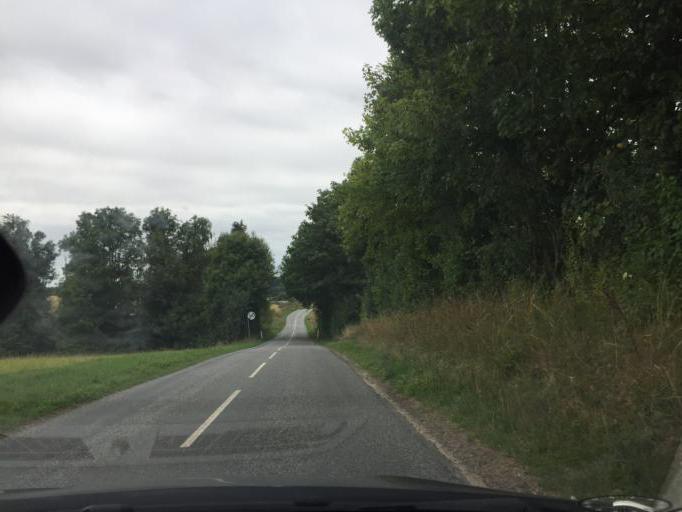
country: DK
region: South Denmark
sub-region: Assens Kommune
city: Arup
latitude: 55.3765
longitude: 10.0789
